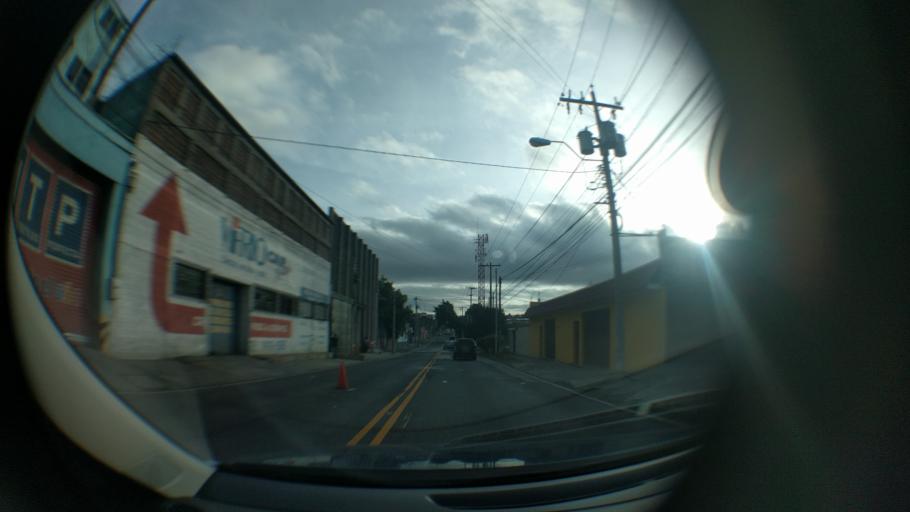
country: GT
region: Guatemala
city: Mixco
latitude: 14.5916
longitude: -90.5583
